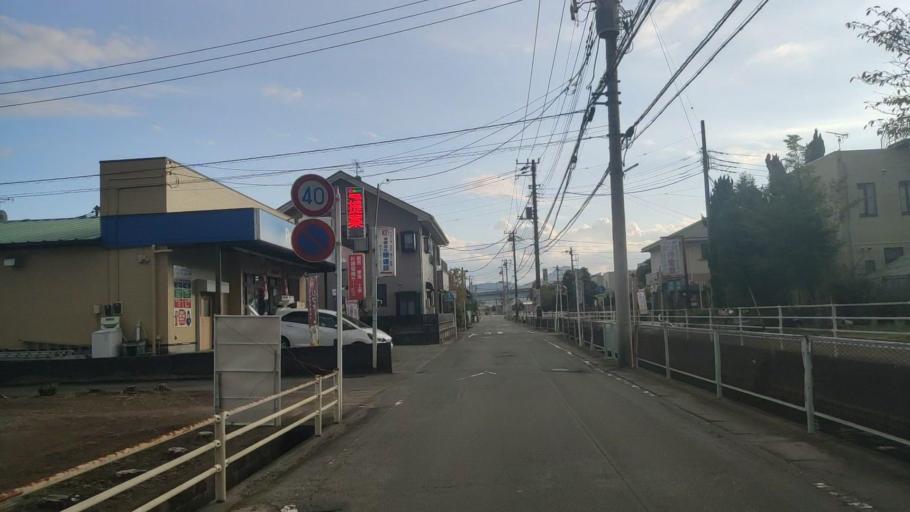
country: JP
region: Shizuoka
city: Mishima
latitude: 35.0932
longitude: 138.9488
